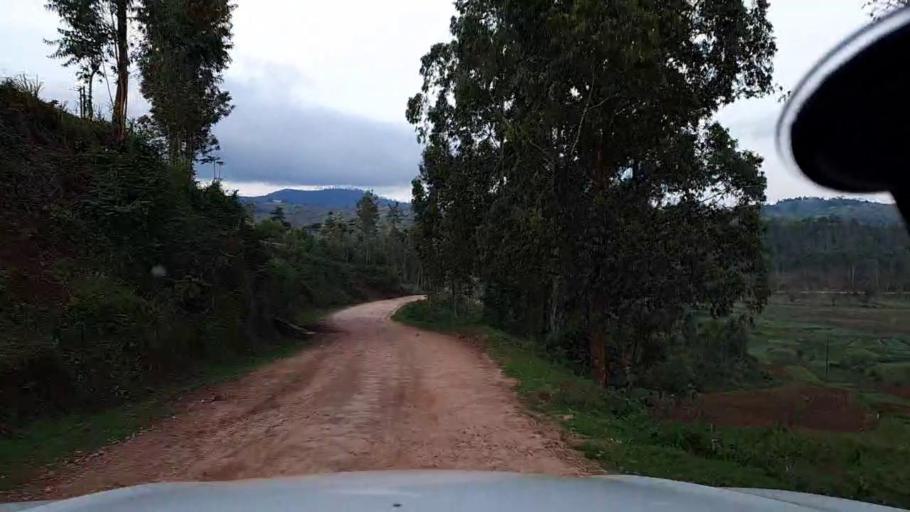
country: RW
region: Southern Province
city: Nyanza
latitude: -2.2114
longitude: 29.6114
